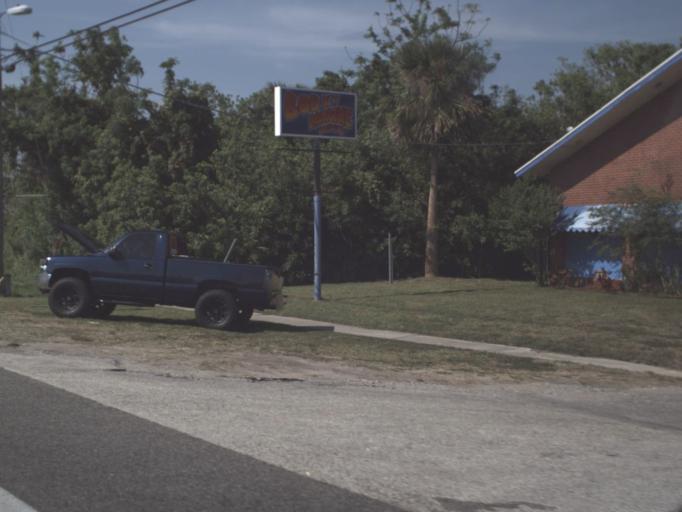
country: US
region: Florida
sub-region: Brevard County
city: Sharpes
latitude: 28.4356
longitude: -80.7610
